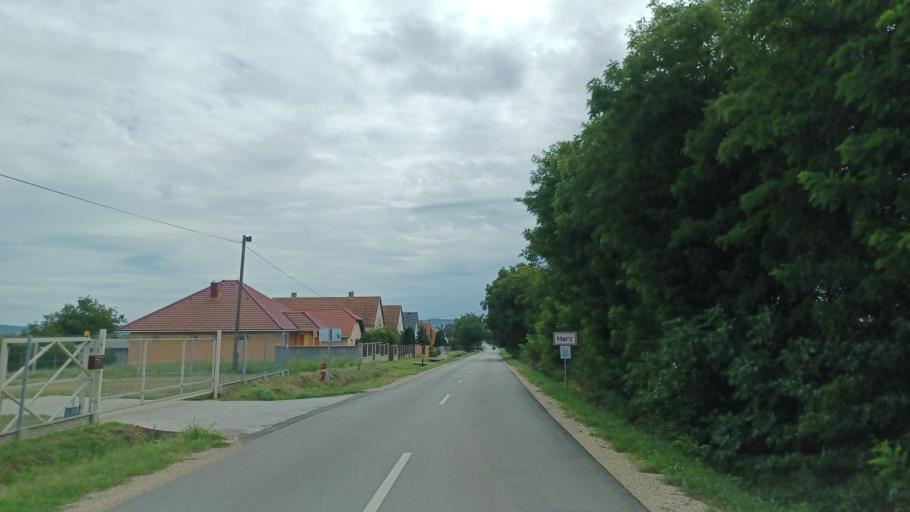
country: HU
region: Tolna
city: Szentgalpuszta
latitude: 46.4069
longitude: 18.6159
